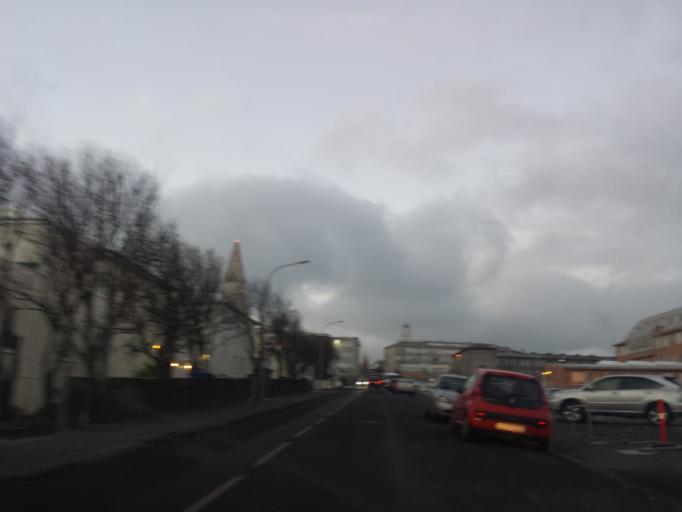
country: IS
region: Capital Region
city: Reykjavik
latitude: 64.1398
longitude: -21.9220
